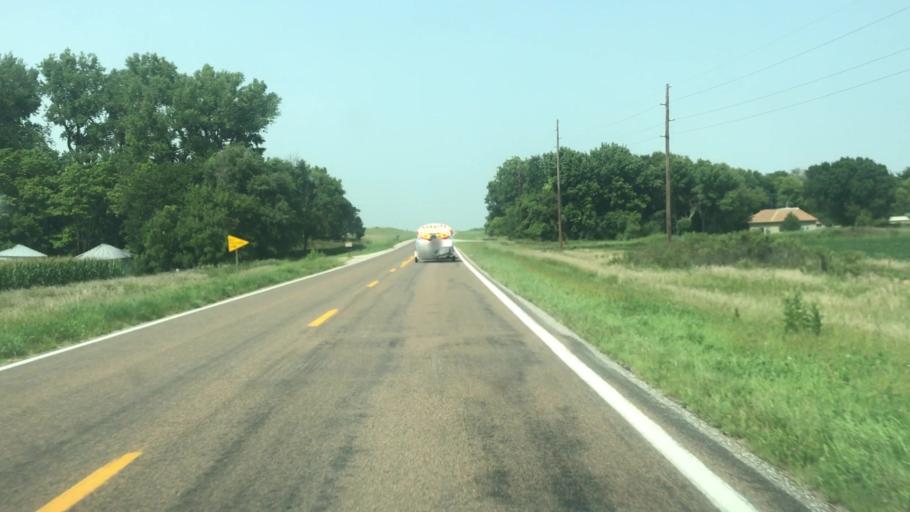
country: US
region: Nebraska
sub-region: Sherman County
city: Loup City
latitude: 41.2477
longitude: -98.9389
